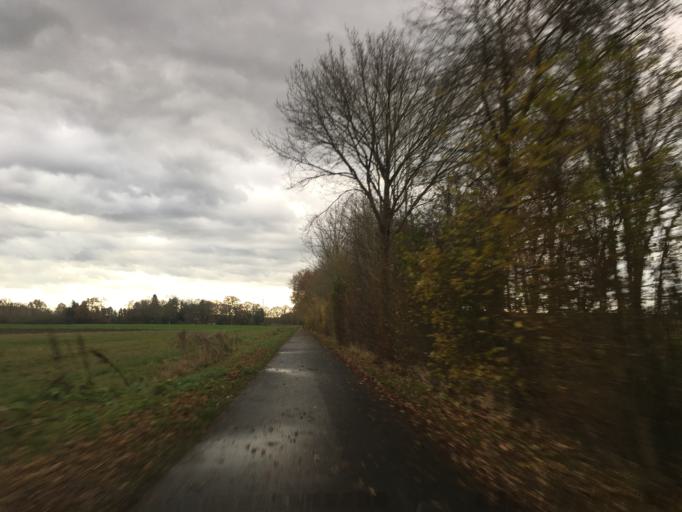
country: DE
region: North Rhine-Westphalia
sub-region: Regierungsbezirk Munster
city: Greven
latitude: 52.0301
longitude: 7.5516
